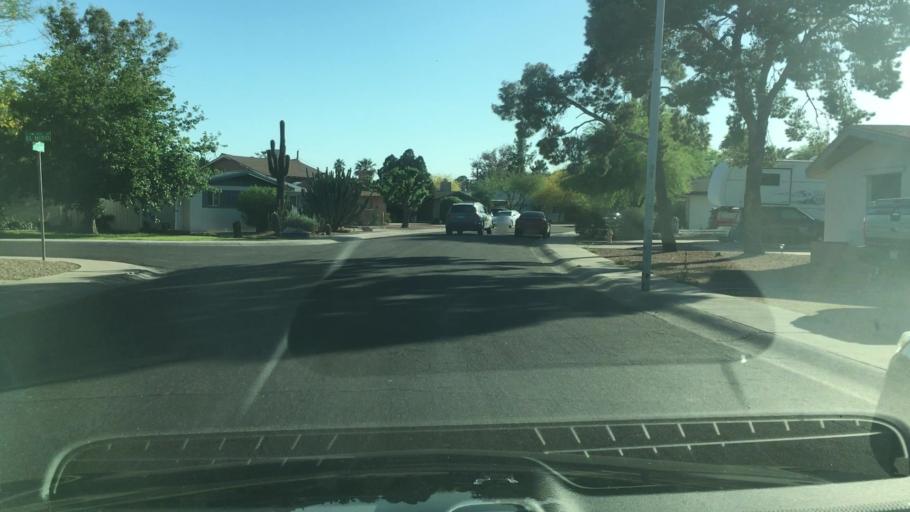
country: US
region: Arizona
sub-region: Maricopa County
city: Scottsdale
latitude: 33.5214
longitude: -111.8934
